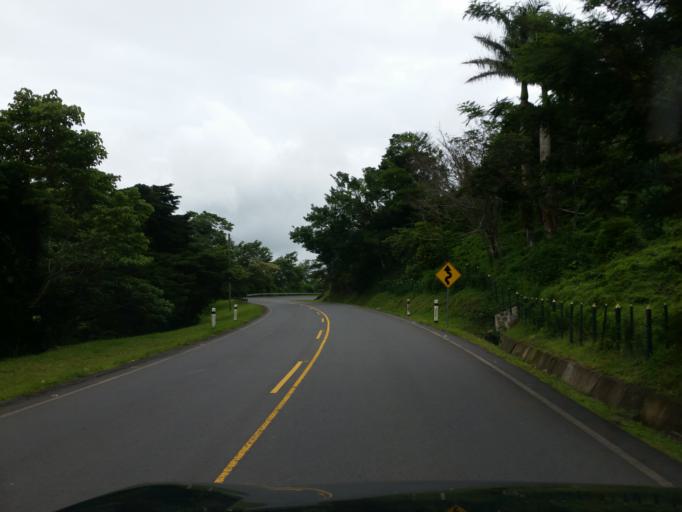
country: NI
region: Matagalpa
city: Matagalpa
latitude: 12.9927
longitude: -85.9195
